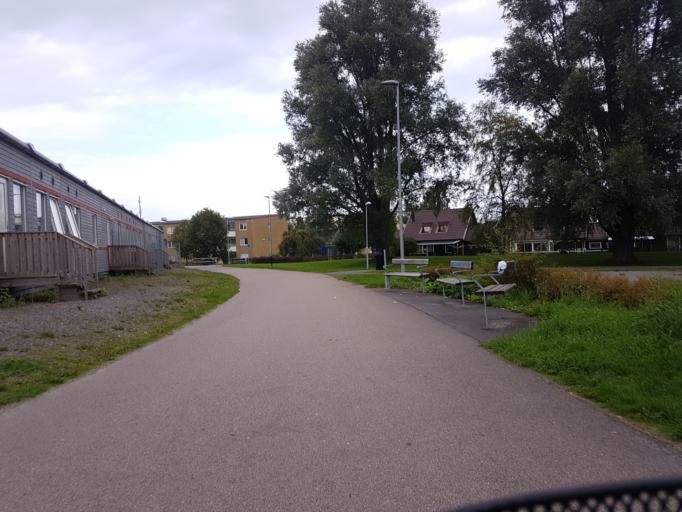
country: SE
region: Vaestra Goetaland
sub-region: Ale Kommun
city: Nodinge-Nol
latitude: 57.8944
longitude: 12.0534
